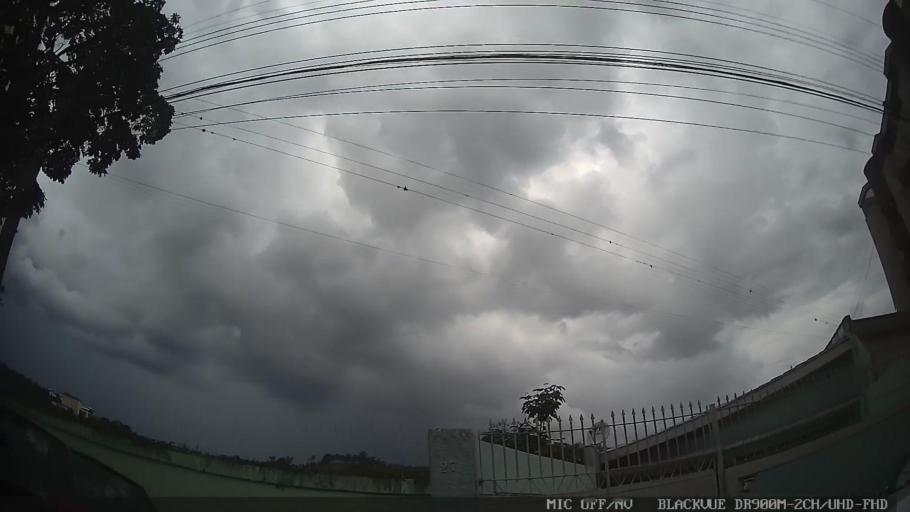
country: BR
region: Sao Paulo
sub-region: Serra Negra
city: Serra Negra
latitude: -22.6136
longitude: -46.7031
